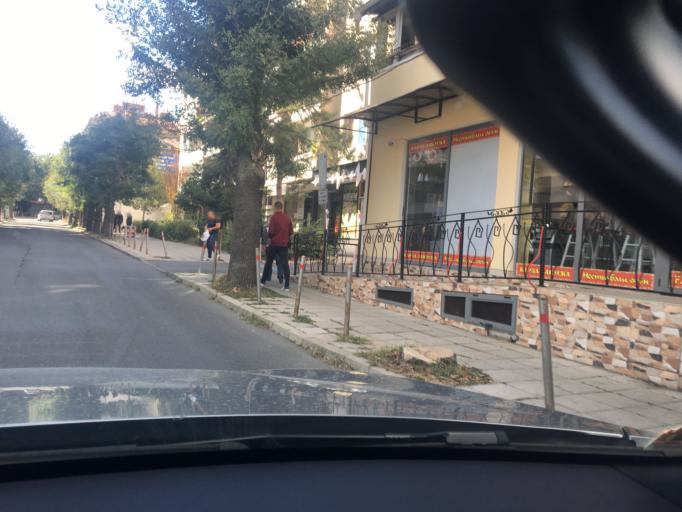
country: BG
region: Burgas
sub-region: Obshtina Burgas
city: Burgas
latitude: 42.4988
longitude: 27.4701
